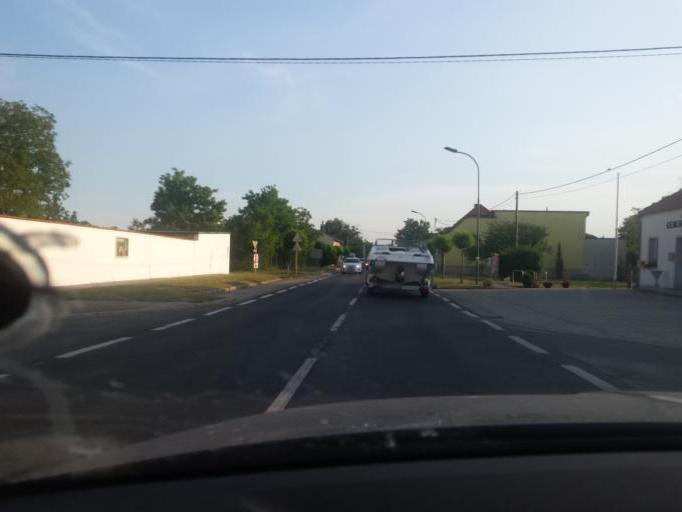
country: AT
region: Lower Austria
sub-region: Politischer Bezirk Bruck an der Leitha
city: Rohrau
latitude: 48.0480
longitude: 16.8329
